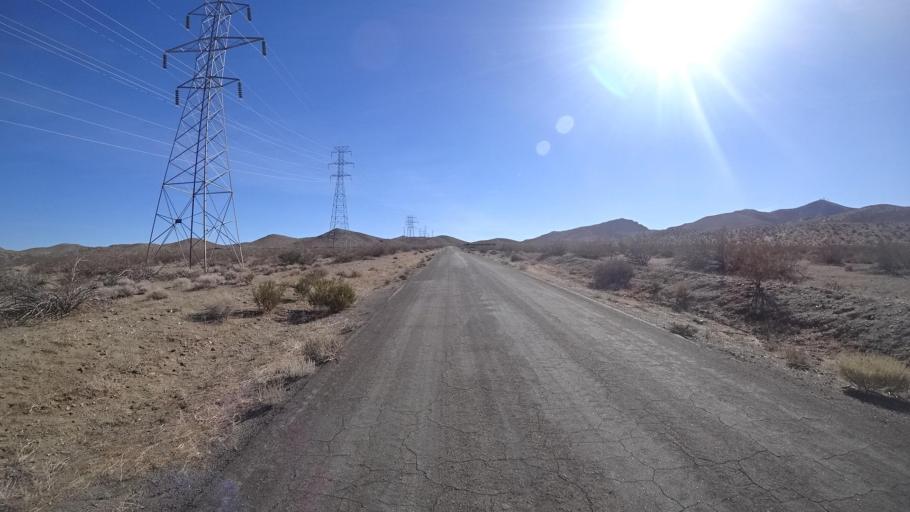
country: US
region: California
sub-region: Kern County
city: Ridgecrest
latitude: 35.3813
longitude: -117.6604
